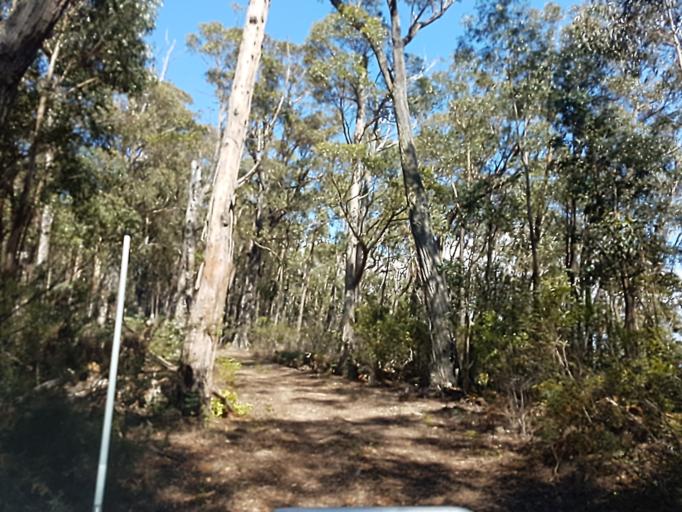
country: AU
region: Victoria
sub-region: East Gippsland
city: Lakes Entrance
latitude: -37.2895
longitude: 148.3252
